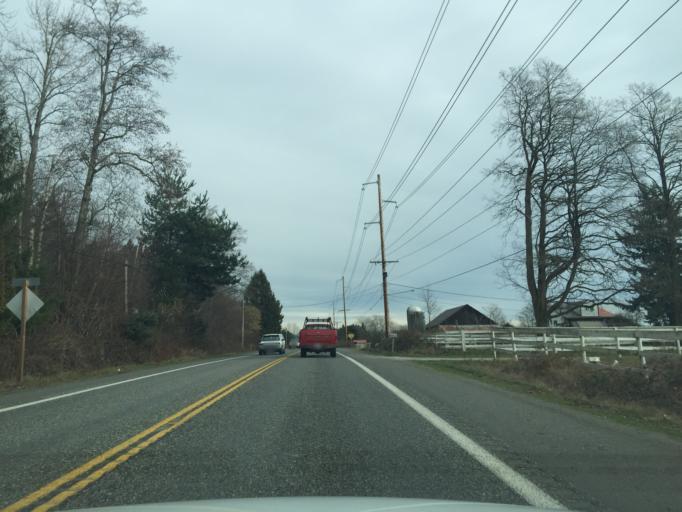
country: US
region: Washington
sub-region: Whatcom County
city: Birch Bay
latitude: 48.9354
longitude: -122.6752
